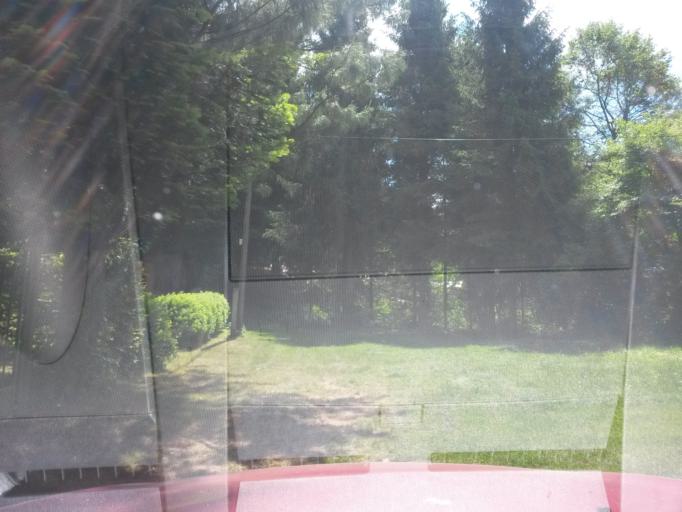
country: SK
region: Kosicky
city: Kosice
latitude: 48.7365
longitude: 21.1197
